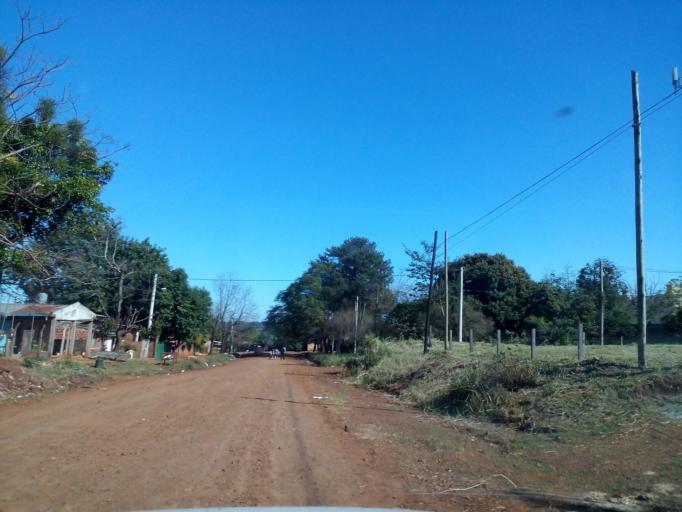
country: AR
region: Misiones
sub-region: Departamento de Capital
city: Posadas
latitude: -27.3759
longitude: -55.9467
